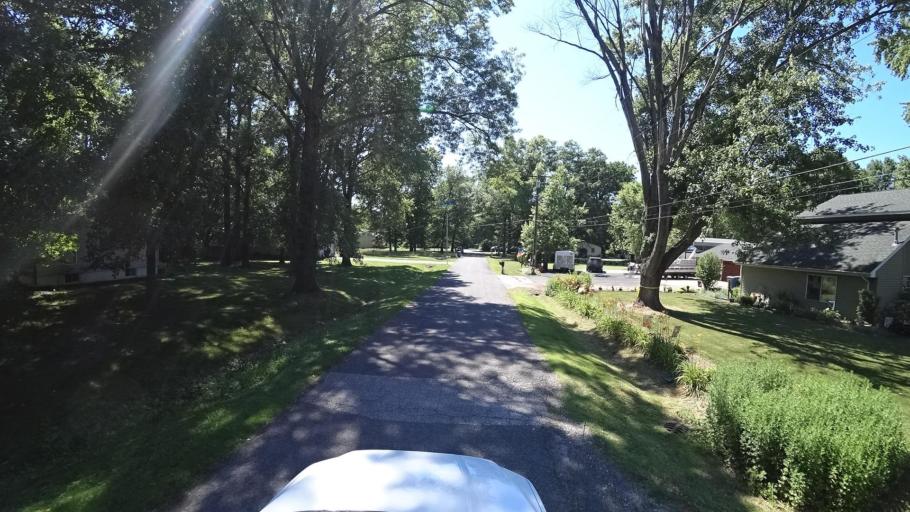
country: US
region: Indiana
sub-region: Porter County
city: Porter
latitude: 41.6048
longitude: -87.0840
